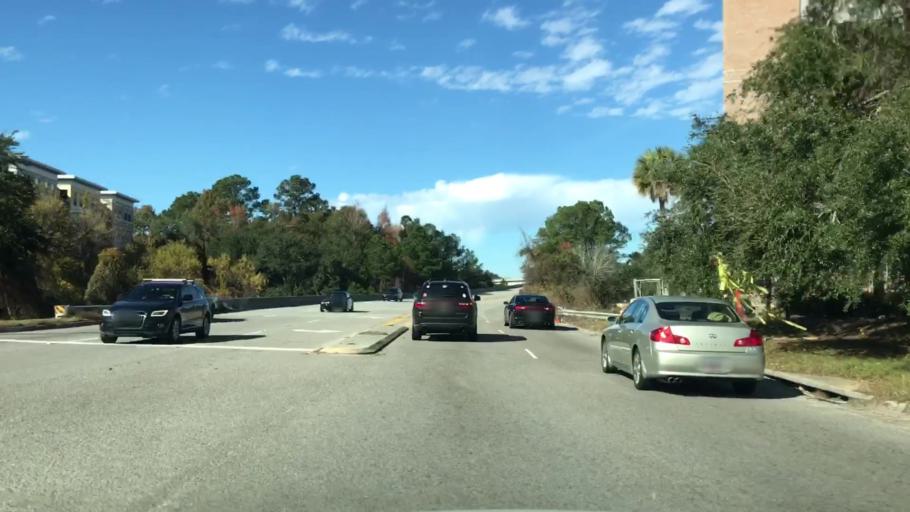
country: US
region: South Carolina
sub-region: Charleston County
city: Charleston
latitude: 32.7771
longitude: -79.9670
